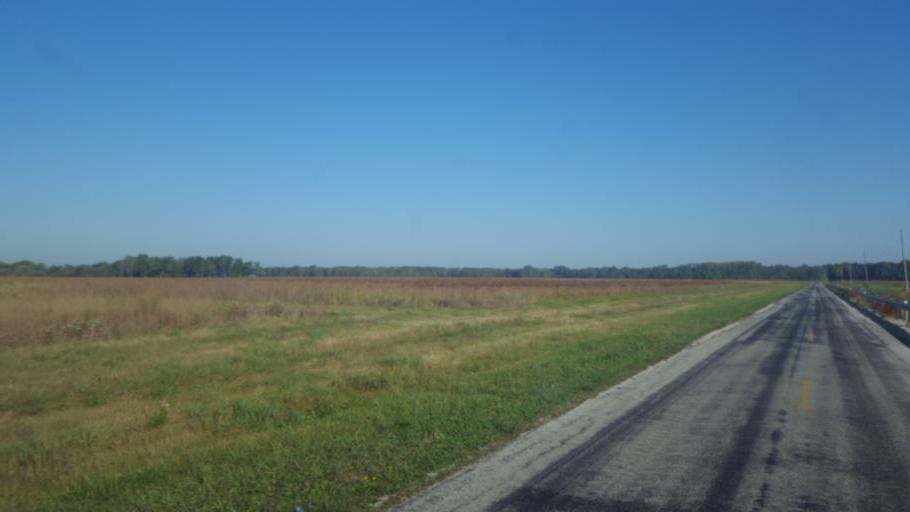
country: US
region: Ohio
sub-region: Union County
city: Richwood
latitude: 40.5513
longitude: -83.3179
